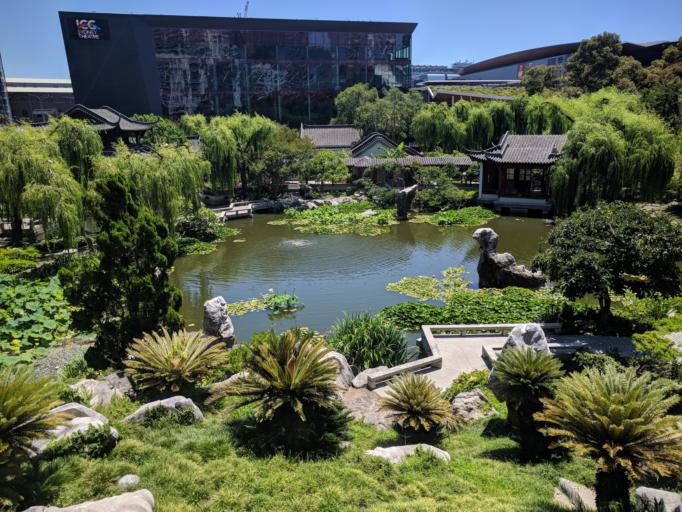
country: AU
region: New South Wales
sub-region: City of Sydney
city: Haymarket
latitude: -33.8758
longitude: 151.2038
